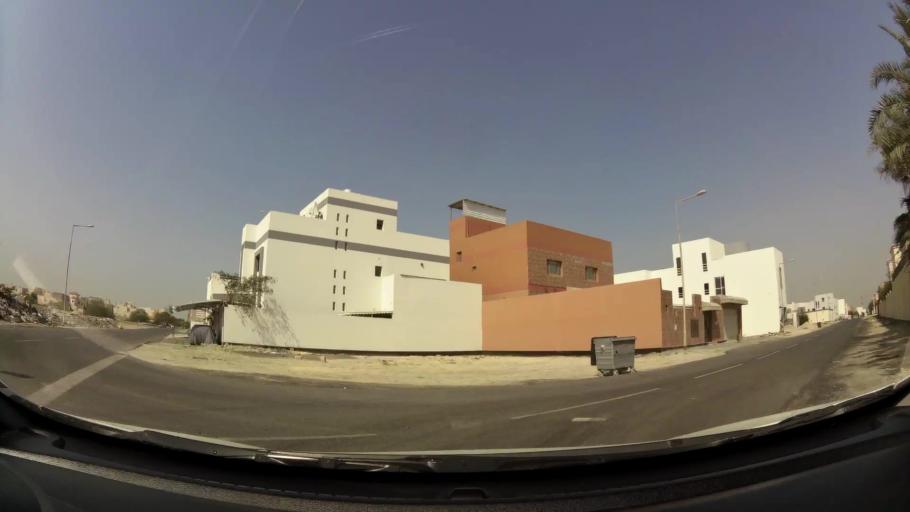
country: BH
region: Manama
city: Jidd Hafs
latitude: 26.2050
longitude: 50.4652
